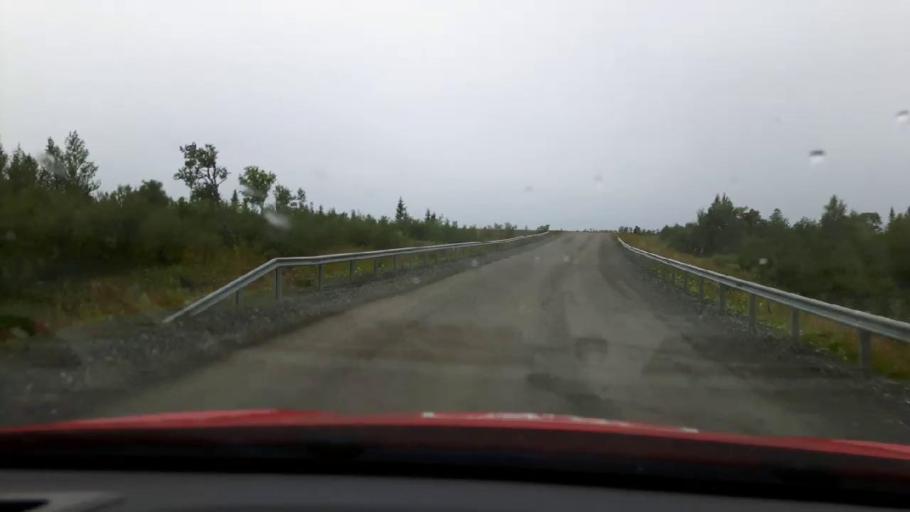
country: NO
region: Nord-Trondelag
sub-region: Meraker
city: Meraker
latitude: 63.6169
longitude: 12.2879
